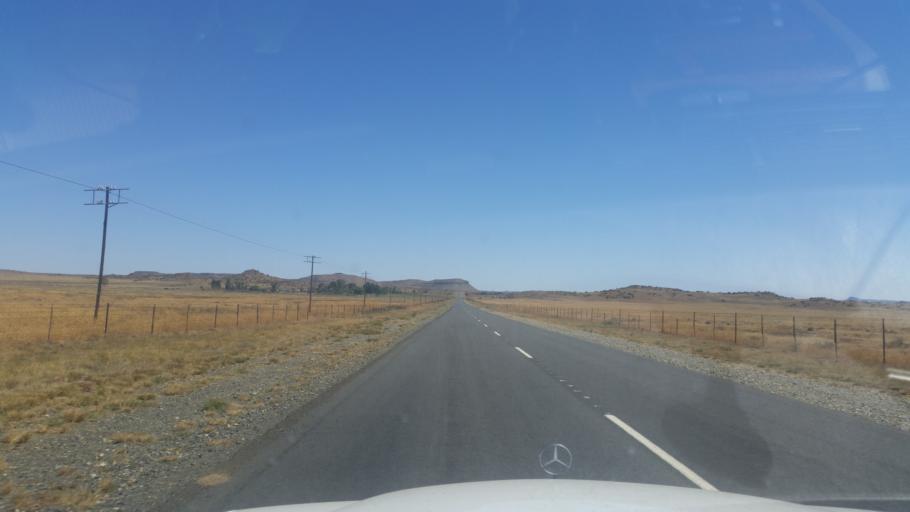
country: ZA
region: Northern Cape
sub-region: Pixley ka Seme District Municipality
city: Colesberg
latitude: -30.7629
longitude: 25.7281
